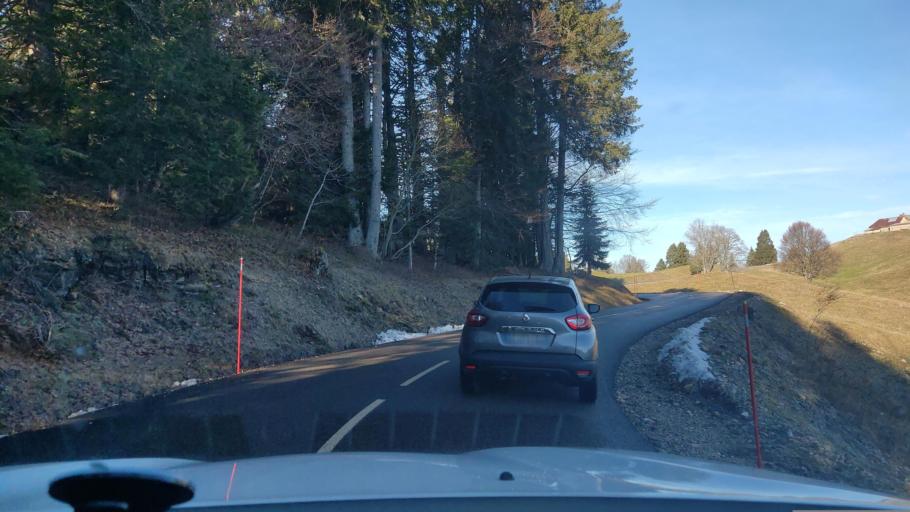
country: FR
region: Rhone-Alpes
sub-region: Departement de la Savoie
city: Mouxy
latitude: 45.6685
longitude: 5.9743
